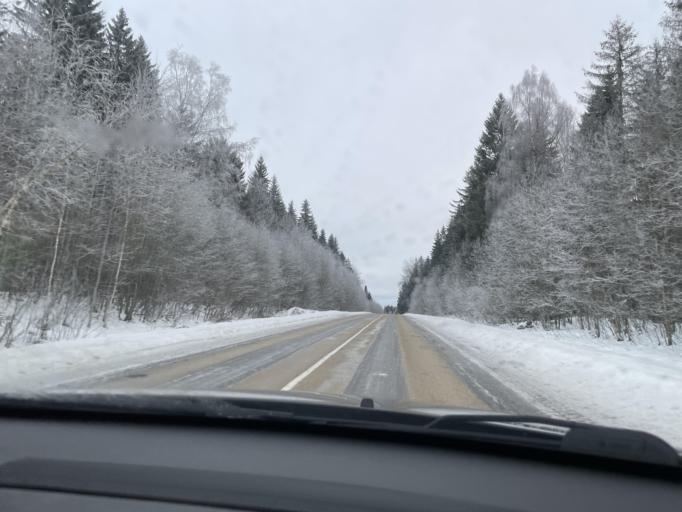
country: LV
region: Rezekne
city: Rezekne
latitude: 56.5000
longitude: 27.3834
